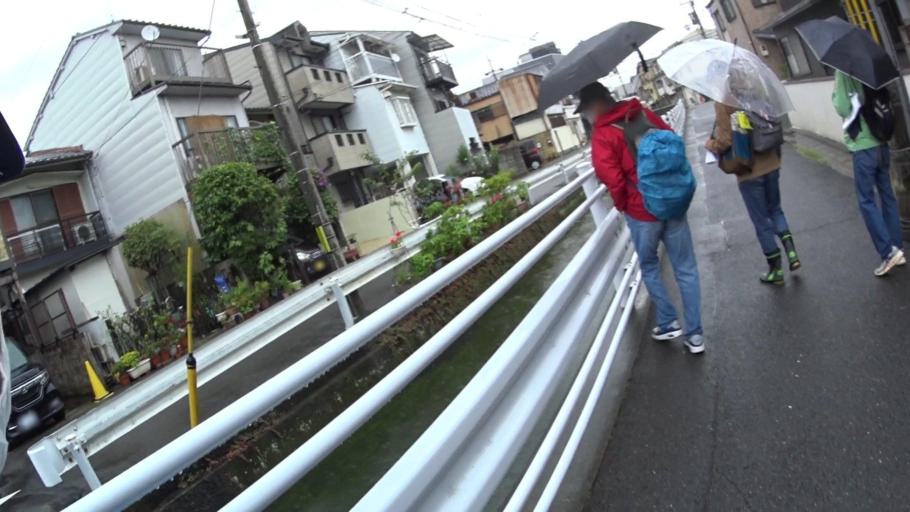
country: JP
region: Kyoto
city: Muko
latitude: 35.0124
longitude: 135.6969
